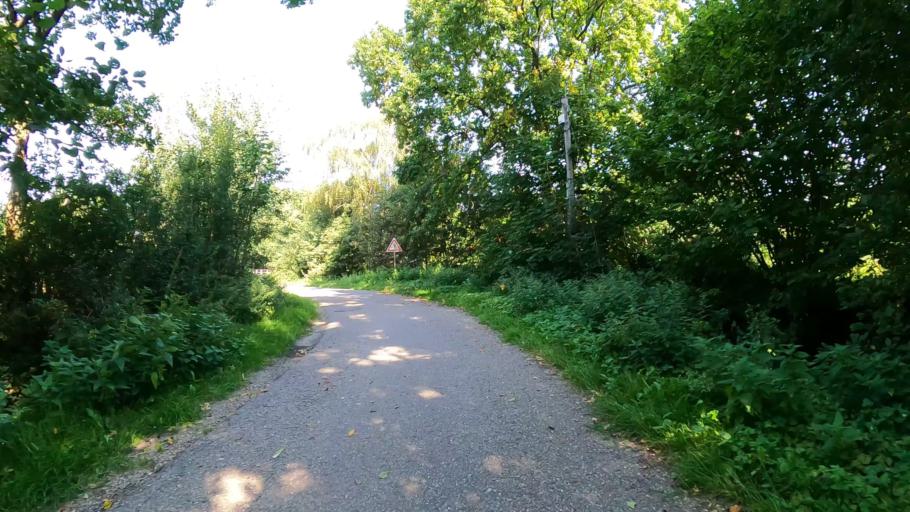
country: DE
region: Schleswig-Holstein
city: Kaltenkirchen
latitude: 53.8248
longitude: 9.9567
